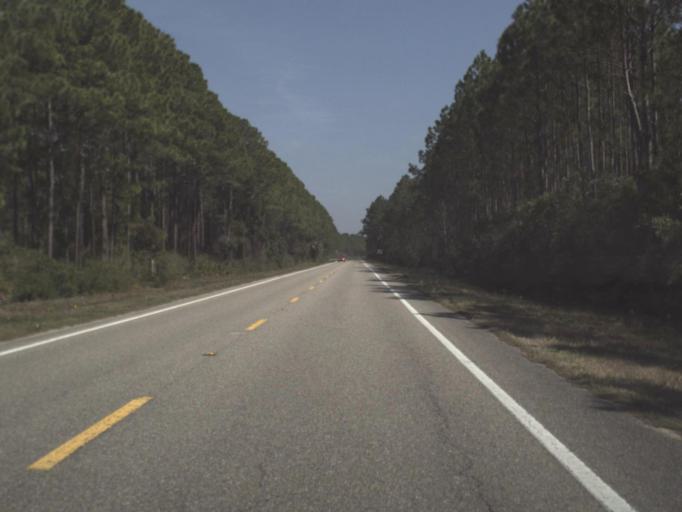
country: US
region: Florida
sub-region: Gulf County
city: Port Saint Joe
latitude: 29.7405
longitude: -85.2030
